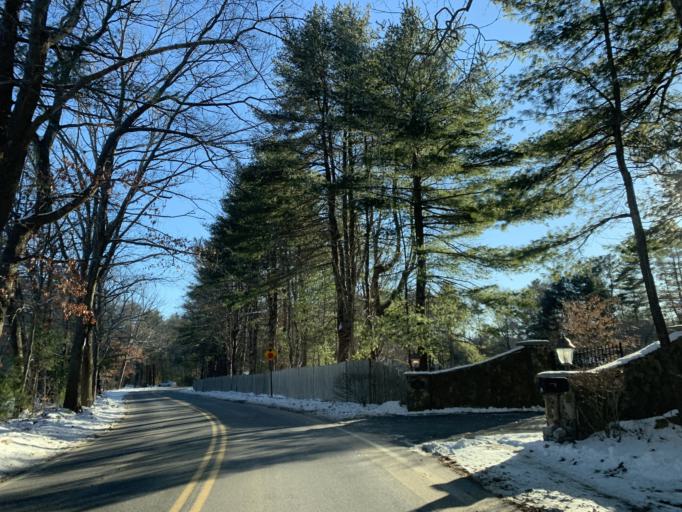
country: US
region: Massachusetts
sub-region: Norfolk County
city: Sharon
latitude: 42.1104
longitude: -71.2107
